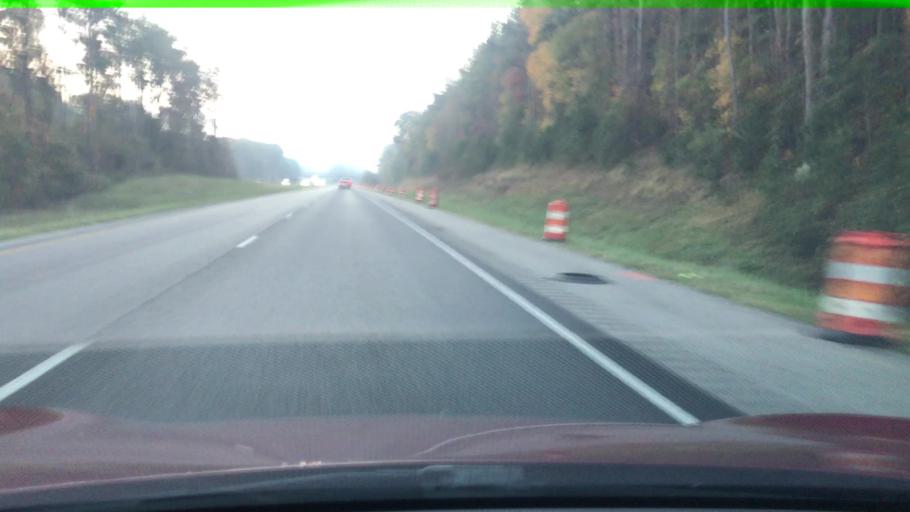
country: US
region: Alabama
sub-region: Chilton County
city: Jemison
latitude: 33.0036
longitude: -86.7052
